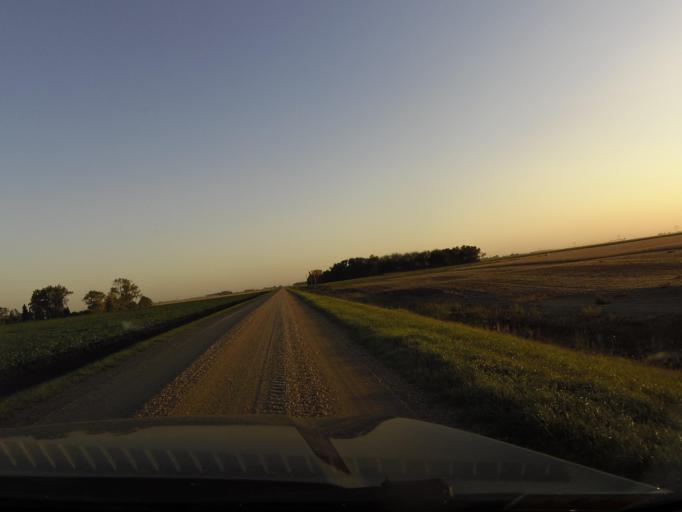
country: US
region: North Dakota
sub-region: Walsh County
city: Grafton
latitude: 48.3856
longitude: -97.2555
